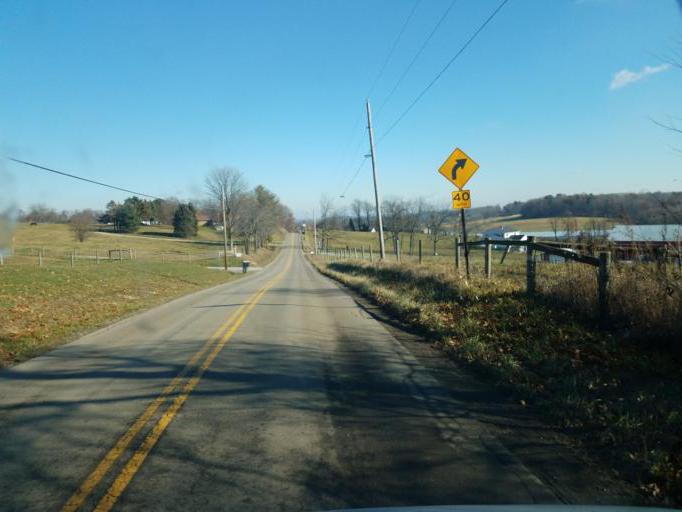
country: US
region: Ohio
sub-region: Stark County
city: Brewster
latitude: 40.6998
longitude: -81.6766
